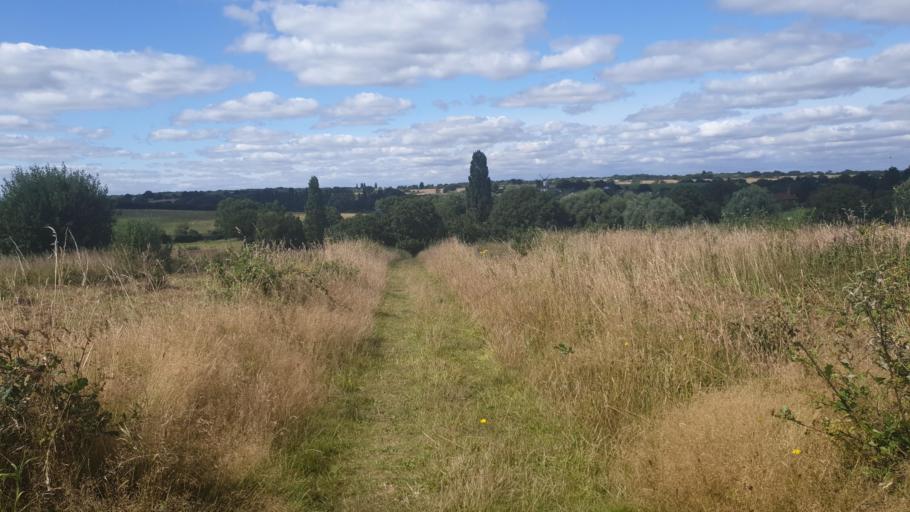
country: GB
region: England
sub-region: Essex
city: Dovercourt
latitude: 51.9216
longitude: 1.2179
